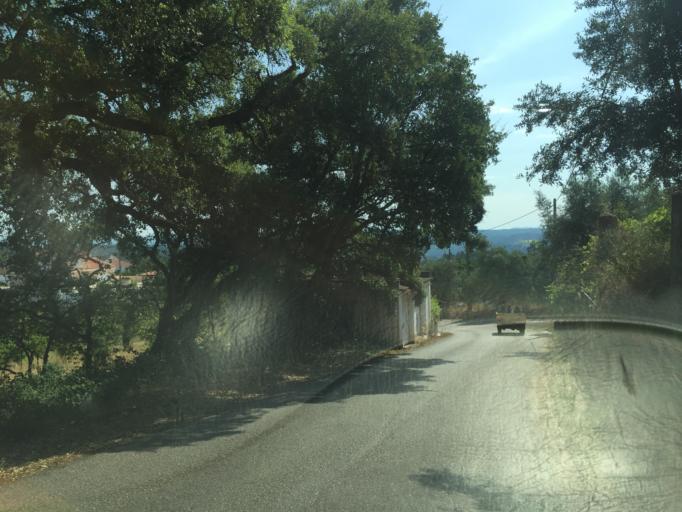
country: PT
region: Santarem
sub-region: Ferreira do Zezere
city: Ferreira do Zezere
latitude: 39.6058
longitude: -8.2888
